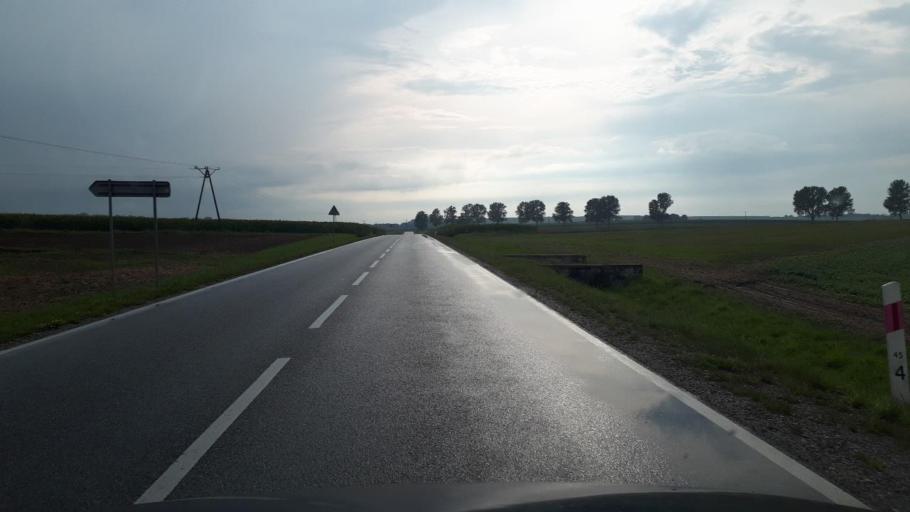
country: PL
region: Silesian Voivodeship
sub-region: Powiat gliwicki
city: Wielowies
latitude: 50.4882
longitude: 18.5690
